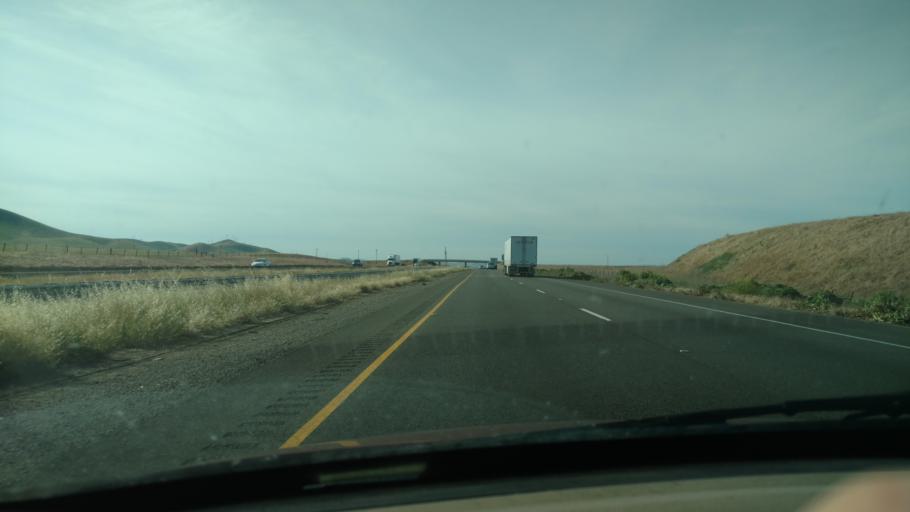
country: US
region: California
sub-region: Merced County
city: Gustine
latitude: 37.1828
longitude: -121.0665
